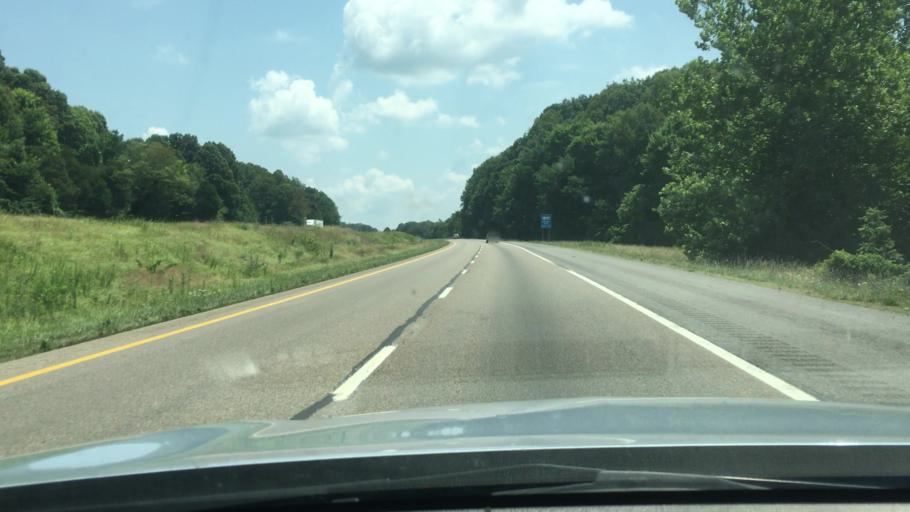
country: US
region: Tennessee
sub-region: Sullivan County
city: Blountville
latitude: 36.5382
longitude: -82.3555
